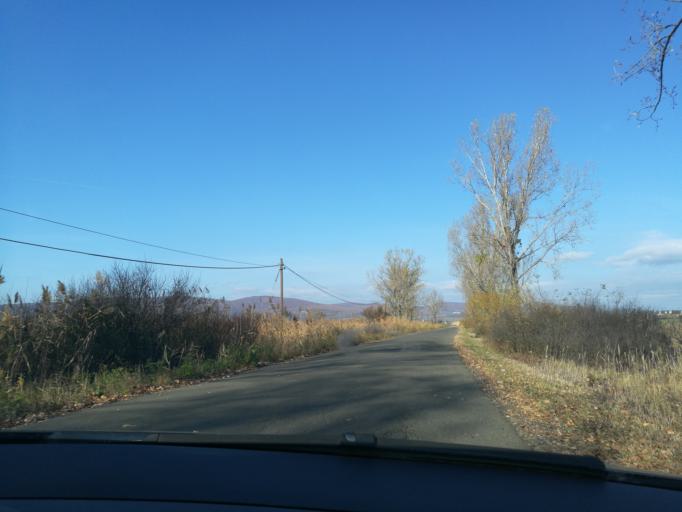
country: HU
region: Nograd
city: Paszto
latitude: 47.9038
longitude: 19.6873
